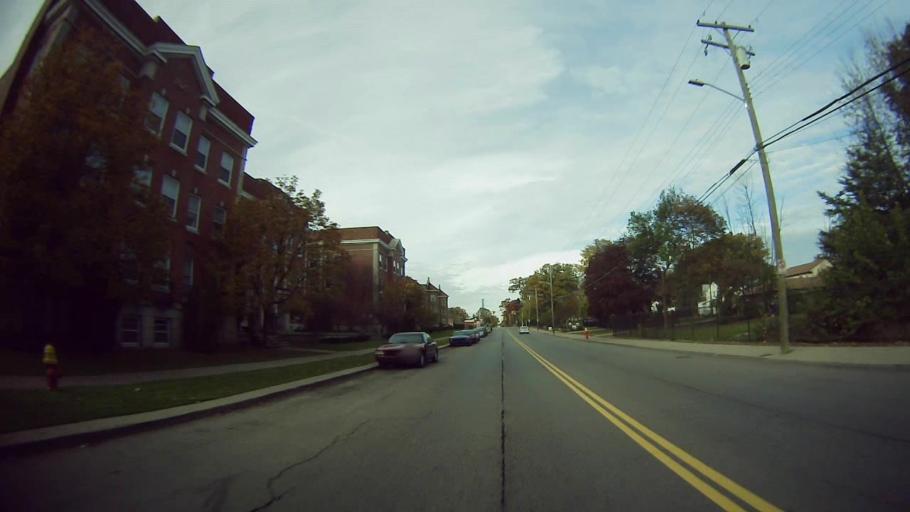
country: US
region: Michigan
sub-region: Wayne County
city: Highland Park
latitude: 42.4175
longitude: -83.1200
